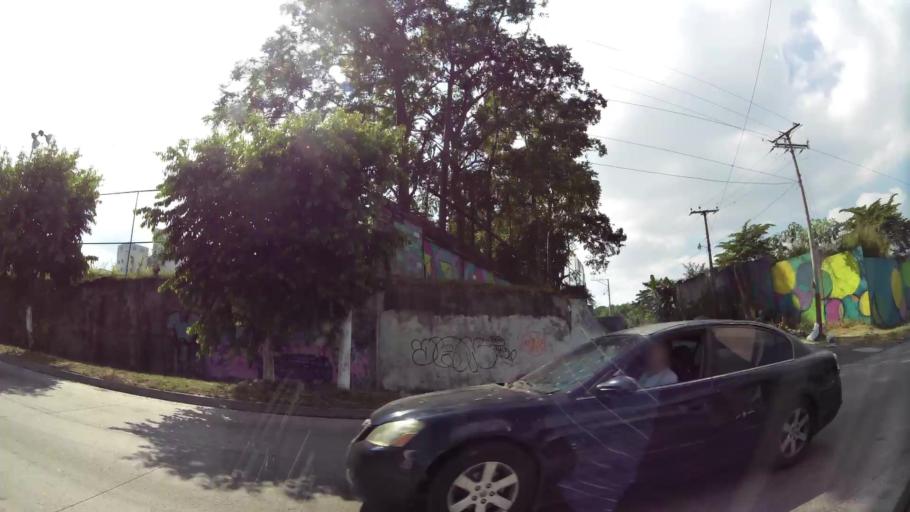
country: SV
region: San Salvador
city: Delgado
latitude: 13.7038
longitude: -89.1713
